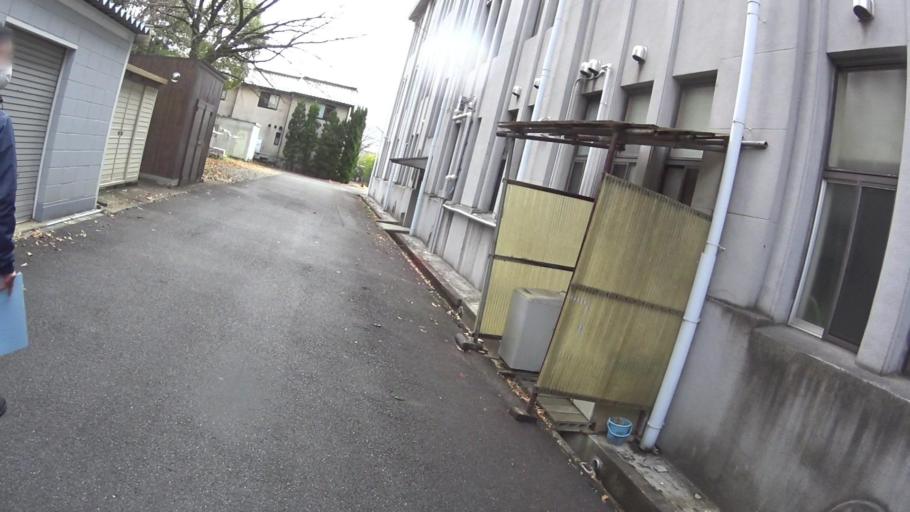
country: JP
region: Kyoto
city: Kyoto
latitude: 34.9875
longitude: 135.7769
